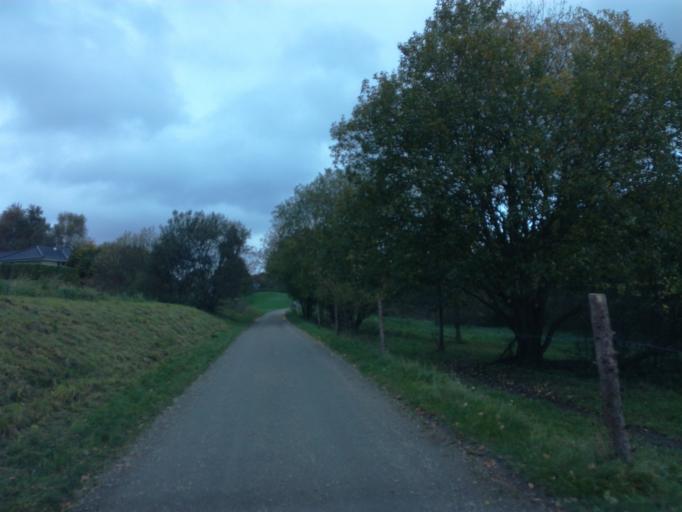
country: DK
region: South Denmark
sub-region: Vejle Kommune
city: Borkop
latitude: 55.6339
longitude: 9.6620
